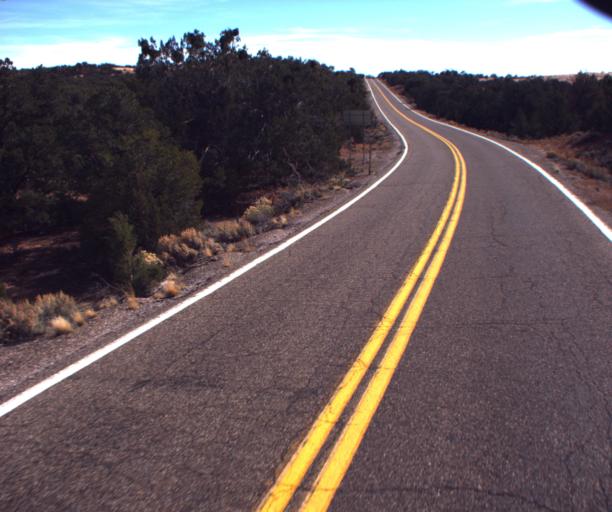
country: US
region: Arizona
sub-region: Navajo County
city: Kayenta
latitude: 36.6707
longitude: -110.5372
